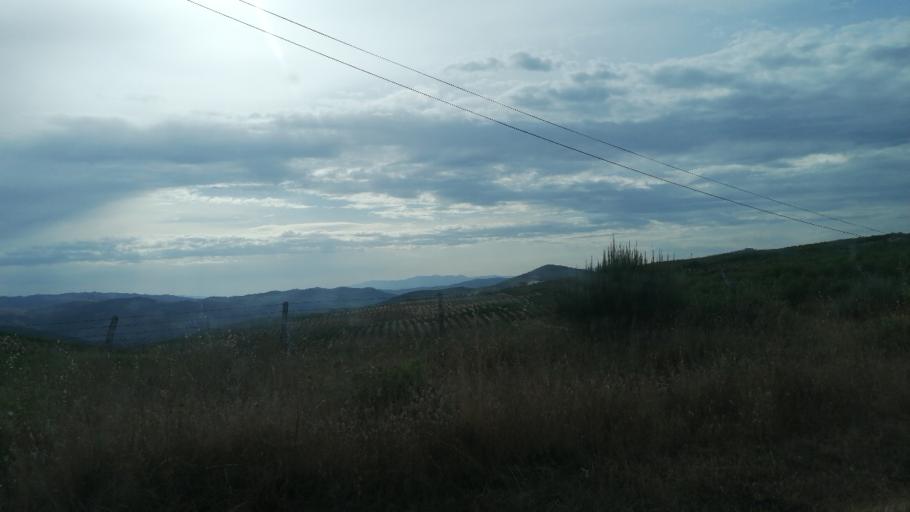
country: PT
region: Viseu
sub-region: Sao Joao da Pesqueira
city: Sao Joao da Pesqueira
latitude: 41.1204
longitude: -7.3900
